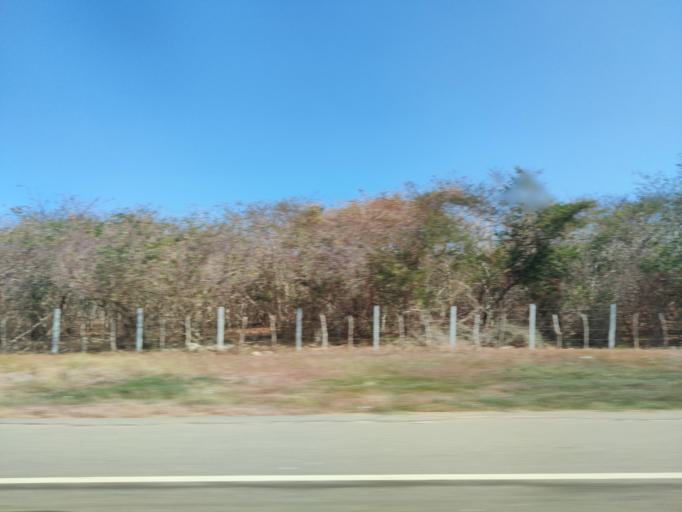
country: CO
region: Atlantico
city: Puerto Colombia
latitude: 10.9680
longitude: -74.9819
